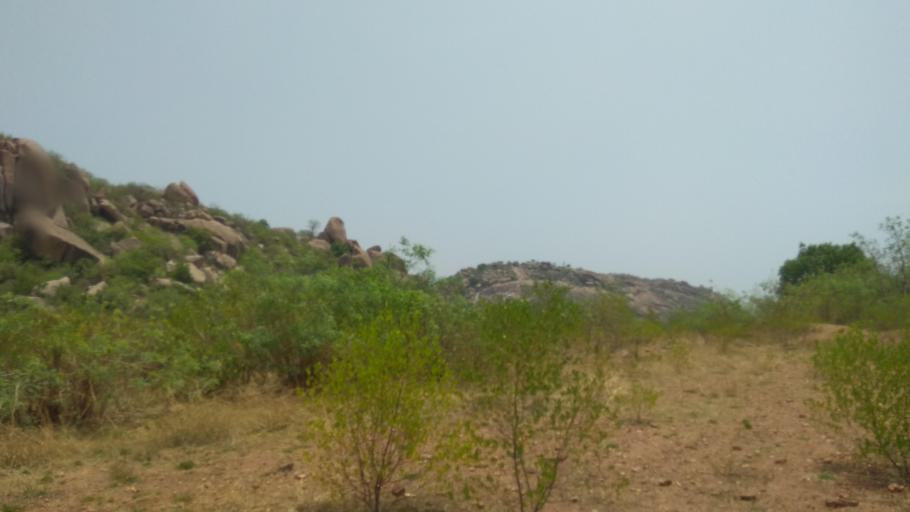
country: IN
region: Telangana
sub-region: Mahbubnagar
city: Farrukhnagar
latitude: 16.8867
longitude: 78.4979
